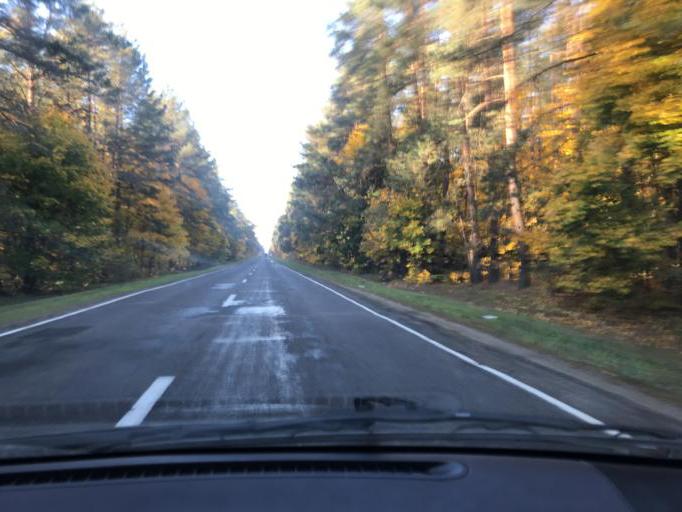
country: BY
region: Brest
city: Tsyelyakhany
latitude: 52.8673
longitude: 25.6997
